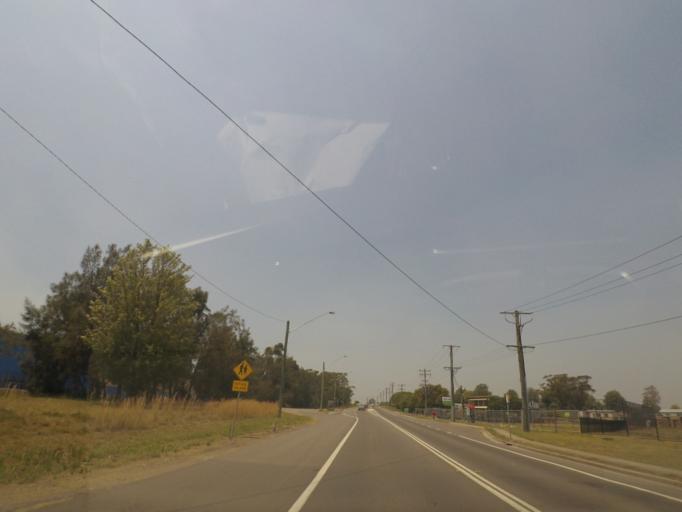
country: AU
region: New South Wales
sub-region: Newcastle
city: Beresfield
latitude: -32.8184
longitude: 151.6978
